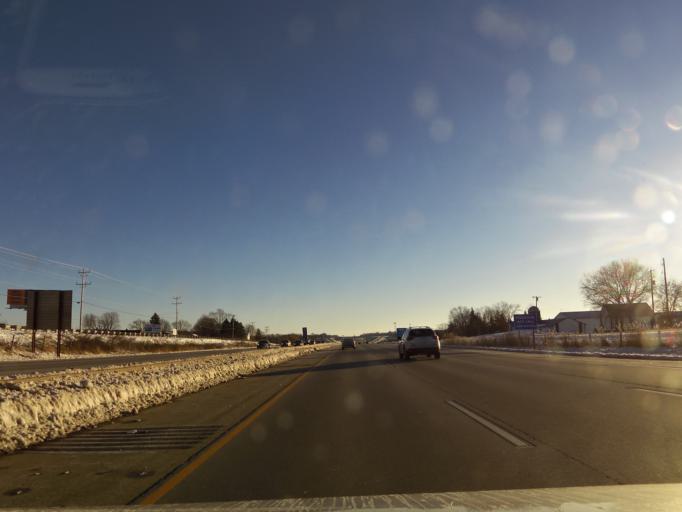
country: US
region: Wisconsin
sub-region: Racine County
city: Caledonia
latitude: 42.8195
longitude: -87.9529
